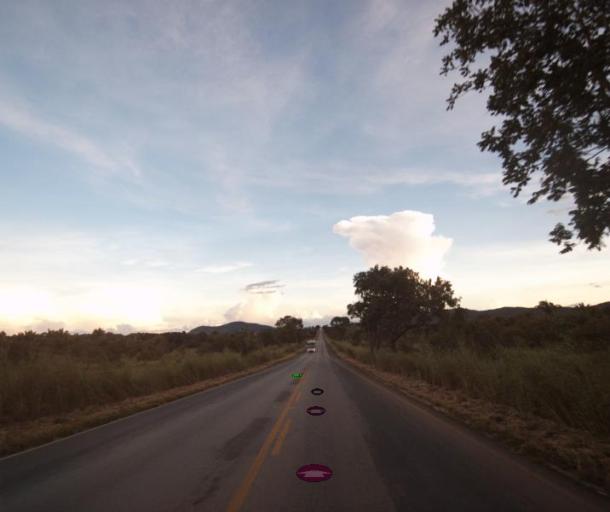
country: BR
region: Goias
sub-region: Uruacu
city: Uruacu
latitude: -14.3558
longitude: -49.1586
